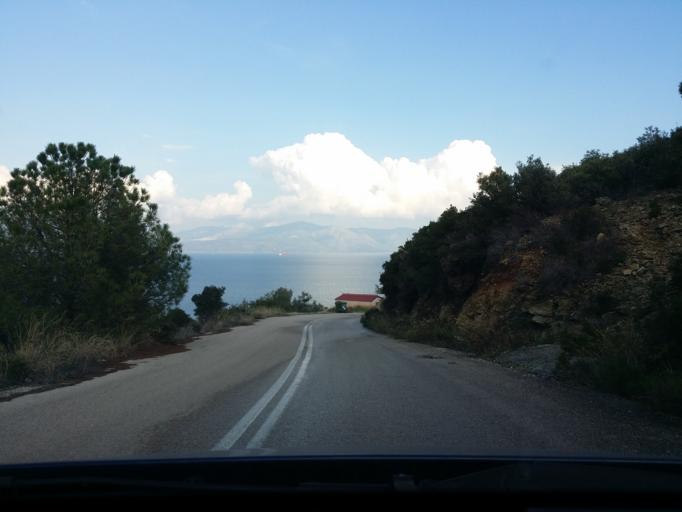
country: GR
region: Attica
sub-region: Nomarchia Anatolikis Attikis
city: Varnavas
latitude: 38.2667
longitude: 23.9686
